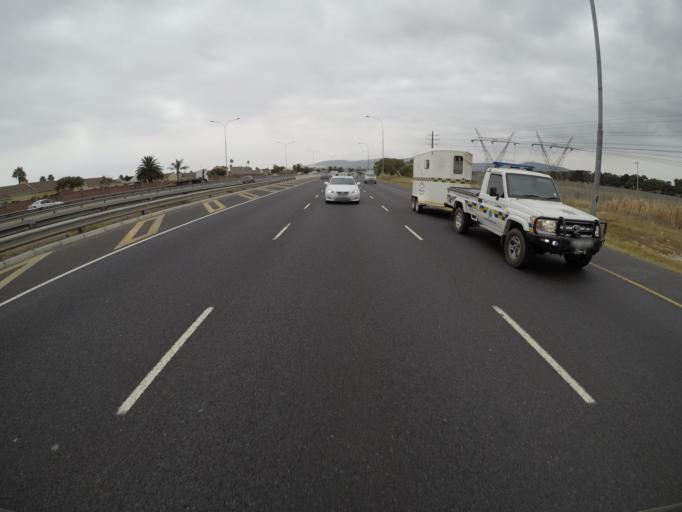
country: ZA
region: Western Cape
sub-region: City of Cape Town
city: Sunset Beach
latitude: -33.8888
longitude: 18.5229
